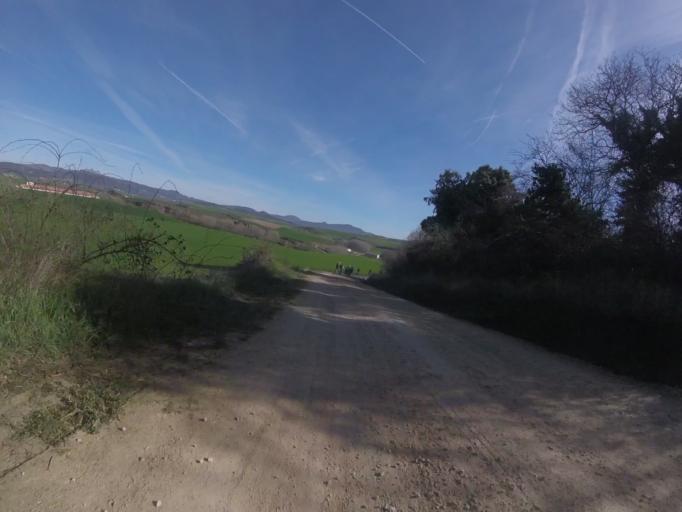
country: ES
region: Navarre
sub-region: Provincia de Navarra
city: Villatuerta
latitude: 42.6923
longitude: -1.9991
